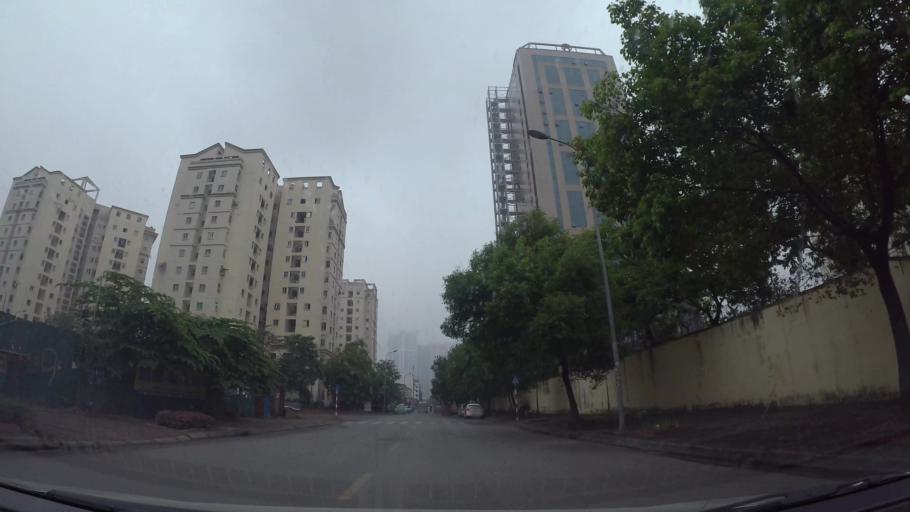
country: VN
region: Ha Noi
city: Thanh Xuan
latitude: 21.0118
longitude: 105.7890
